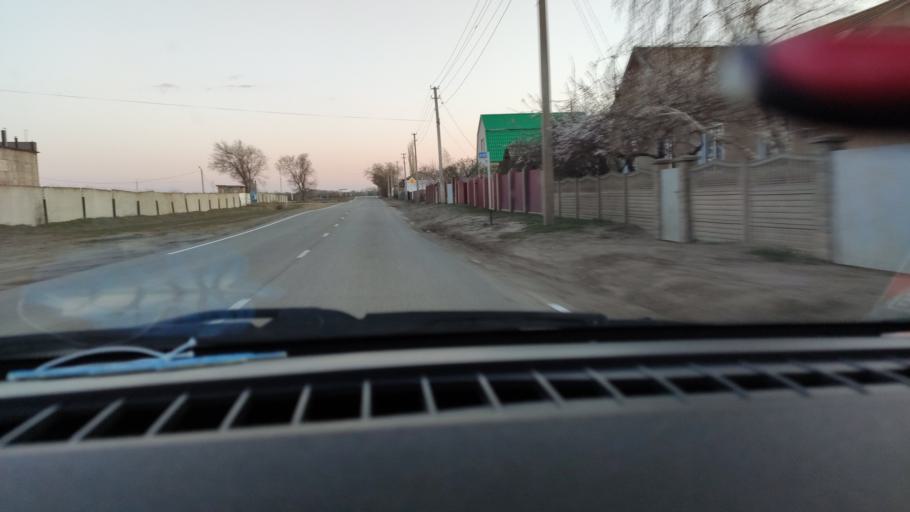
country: RU
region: Saratov
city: Privolzhskiy
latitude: 51.1965
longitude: 45.9154
